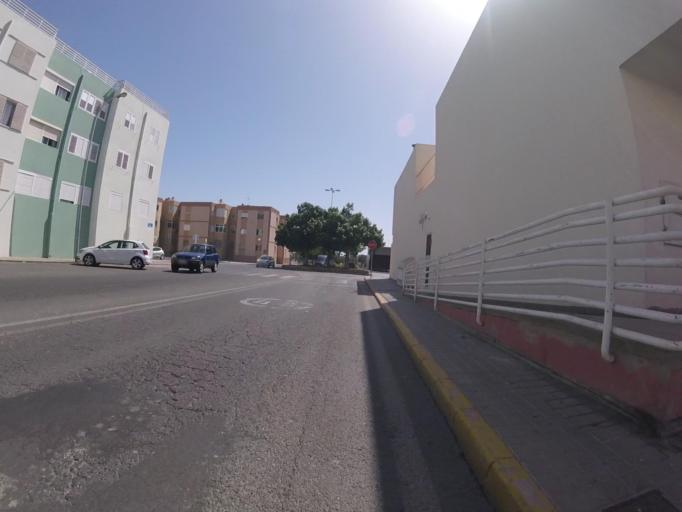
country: ES
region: Canary Islands
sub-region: Provincia de Las Palmas
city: Maspalomas
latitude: 27.7685
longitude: -15.5831
